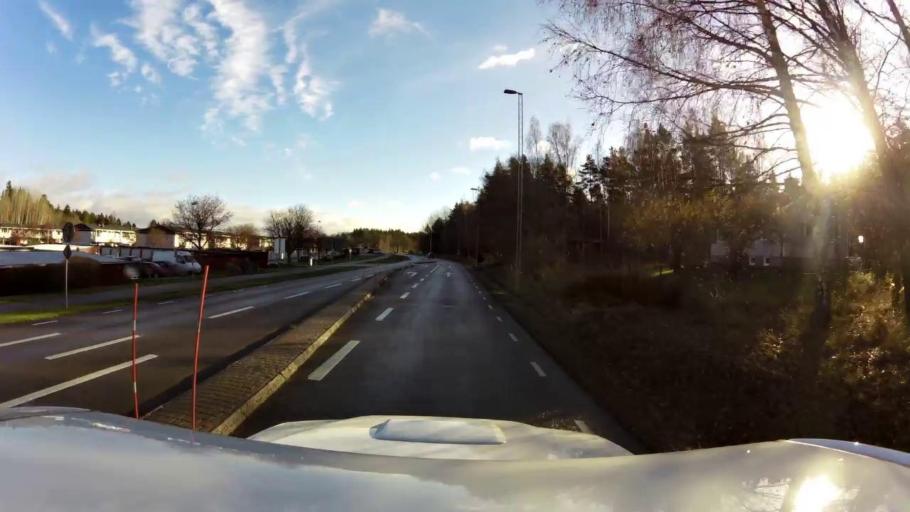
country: SE
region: OEstergoetland
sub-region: Linkopings Kommun
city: Linkoping
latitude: 58.3744
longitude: 15.6450
